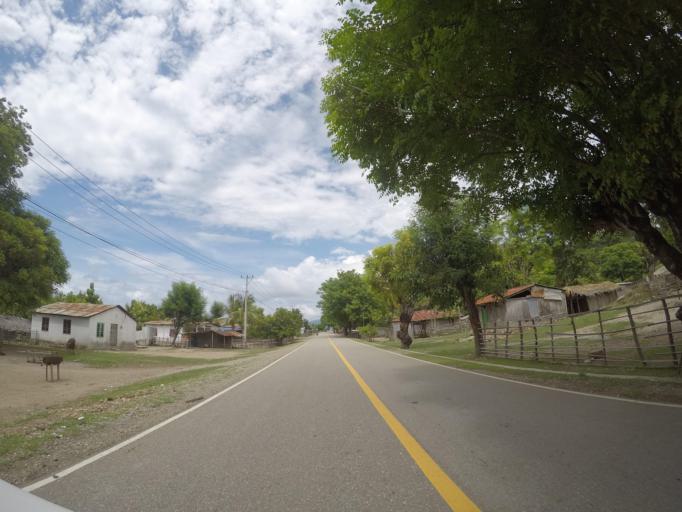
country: TL
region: Bobonaro
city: Maliana
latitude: -8.8228
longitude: 125.0723
